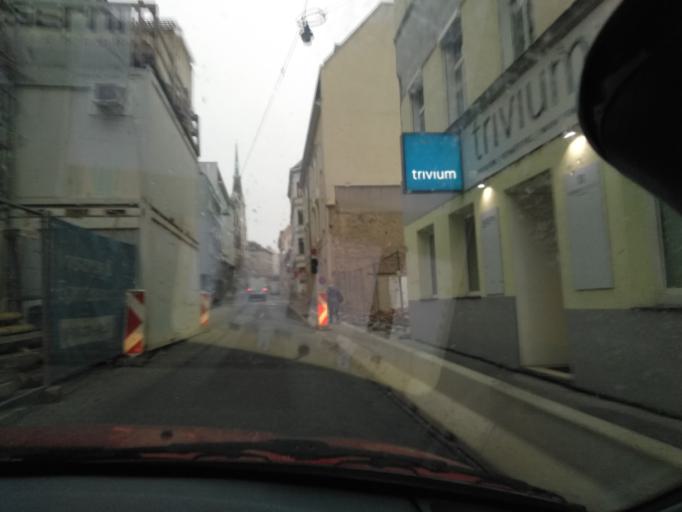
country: AT
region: Vienna
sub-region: Wien Stadt
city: Vienna
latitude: 48.2183
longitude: 16.3395
